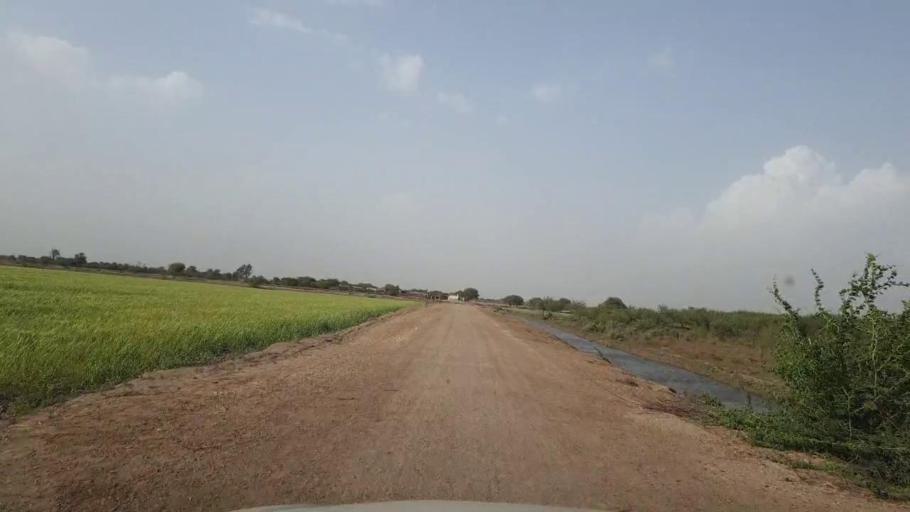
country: PK
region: Sindh
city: Tando Ghulam Ali
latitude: 25.1051
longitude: 68.8619
